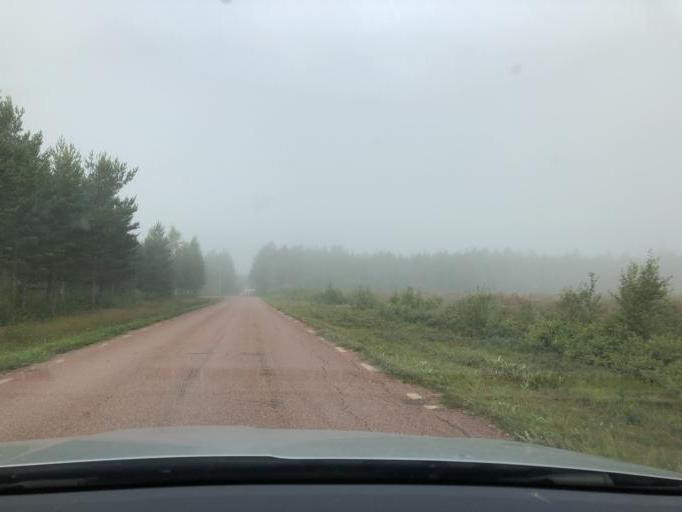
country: SE
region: Dalarna
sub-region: Mora Kommun
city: Mora
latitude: 60.9677
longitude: 14.5009
